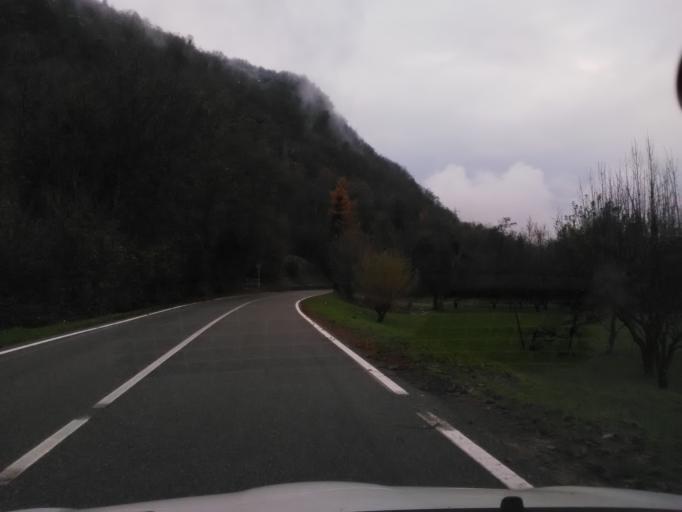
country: IT
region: Piedmont
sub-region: Provincia di Vercelli
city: Quarona
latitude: 45.7715
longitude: 8.2583
